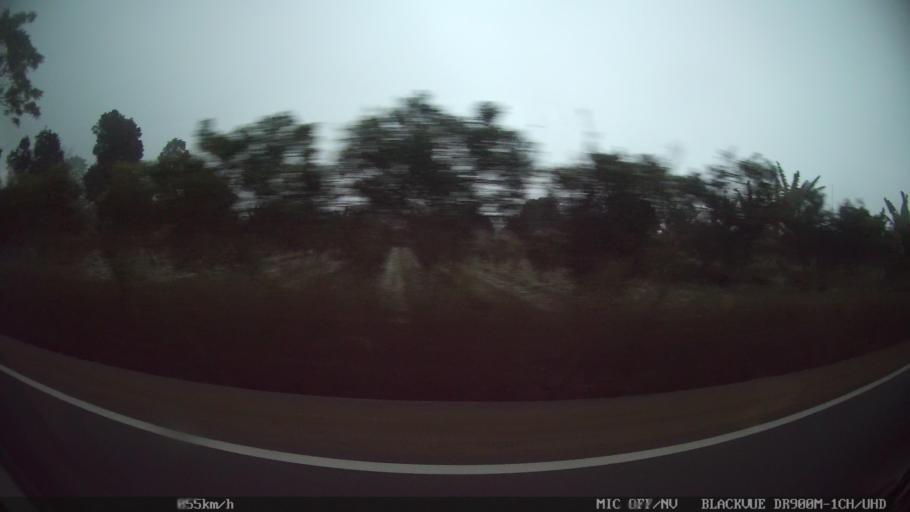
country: ID
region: Bali
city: Banjar Kedisan
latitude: -8.2898
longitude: 115.3181
